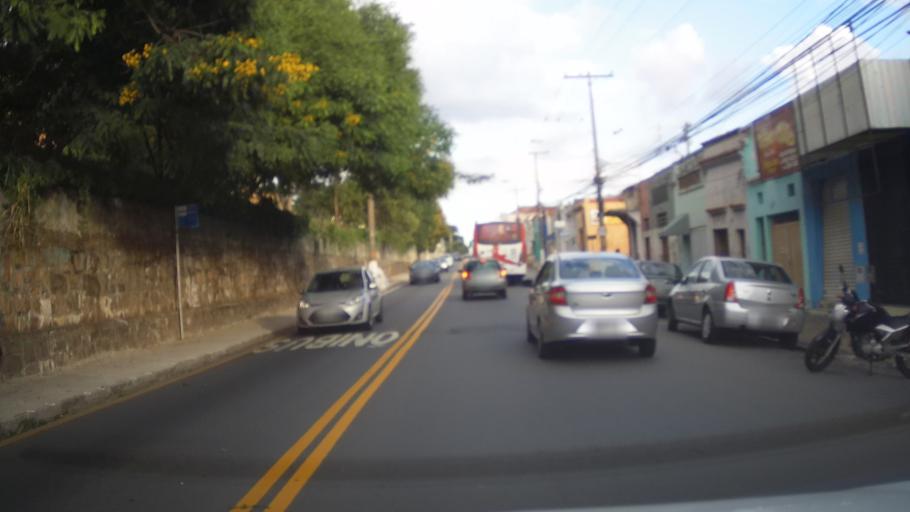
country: BR
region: Sao Paulo
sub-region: Campinas
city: Campinas
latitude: -22.9089
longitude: -47.0748
